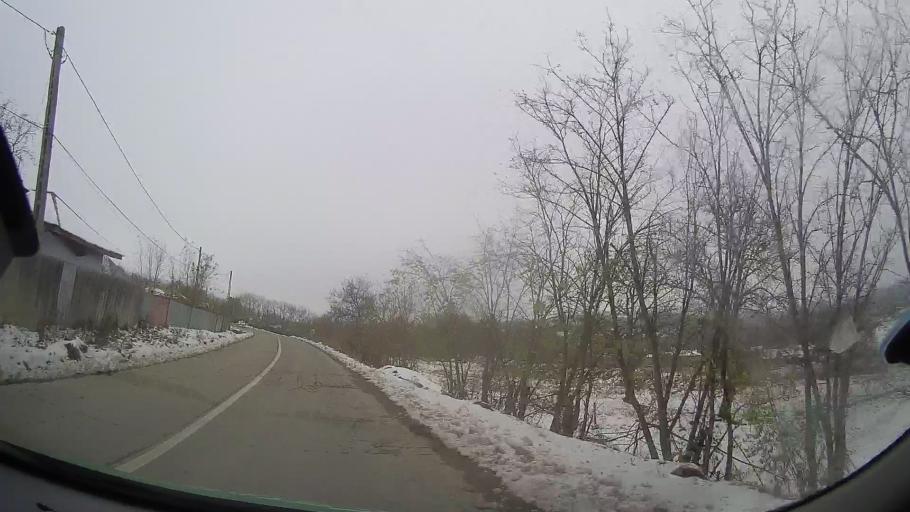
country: RO
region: Vrancea
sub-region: Comuna Boghesti
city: Boghesti
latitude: 46.1992
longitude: 27.4438
